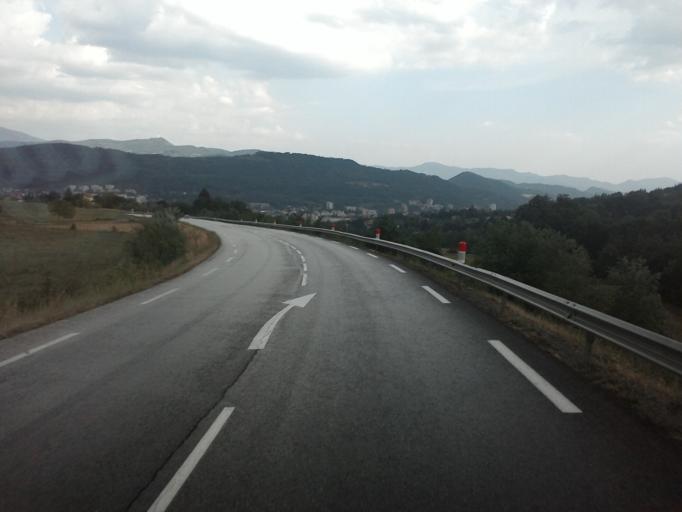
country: FR
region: Provence-Alpes-Cote d'Azur
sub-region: Departement des Hautes-Alpes
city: Gap
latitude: 44.5746
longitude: 6.0743
